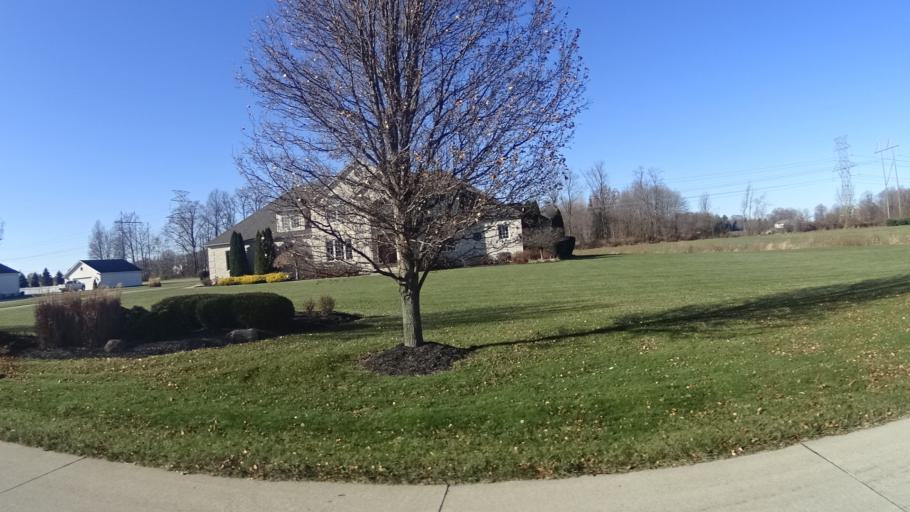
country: US
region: Ohio
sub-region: Lorain County
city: South Amherst
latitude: 41.3834
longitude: -82.2669
